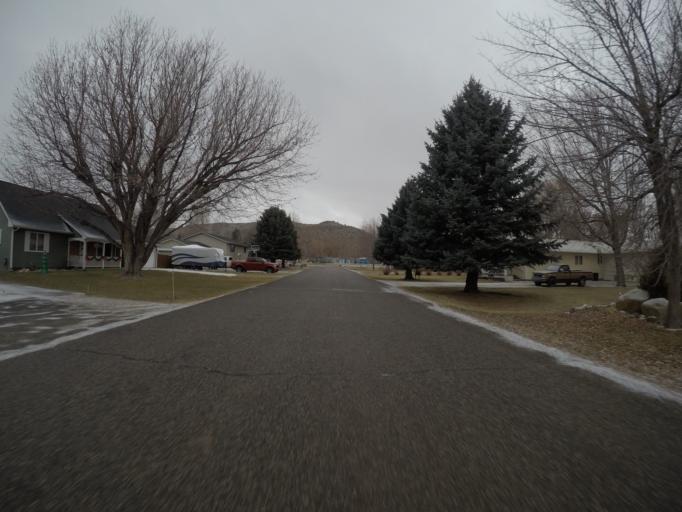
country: US
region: Montana
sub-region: Stillwater County
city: Absarokee
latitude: 45.5226
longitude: -109.4425
